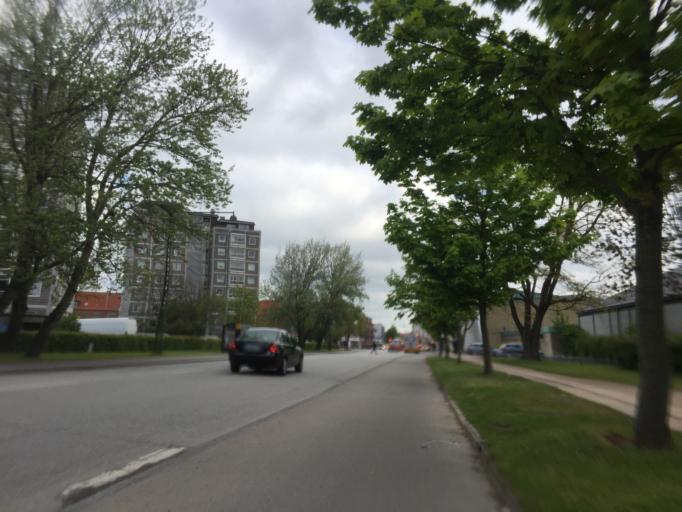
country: DK
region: Capital Region
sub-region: Frederiksberg Kommune
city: Frederiksberg
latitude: 55.7048
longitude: 12.5135
